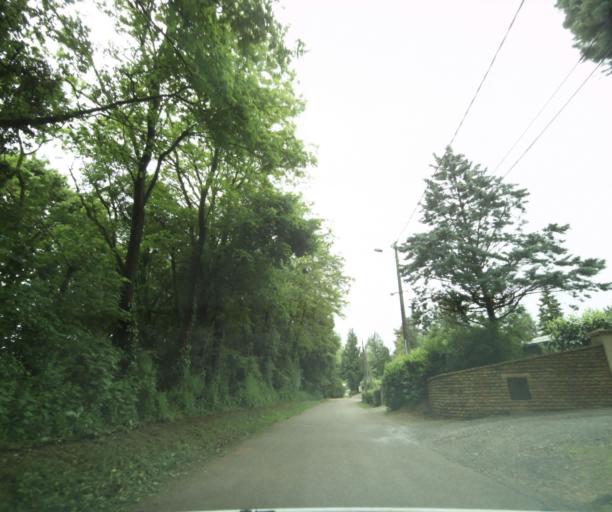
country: FR
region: Bourgogne
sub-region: Departement de Saone-et-Loire
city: Charolles
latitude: 46.4392
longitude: 4.2761
